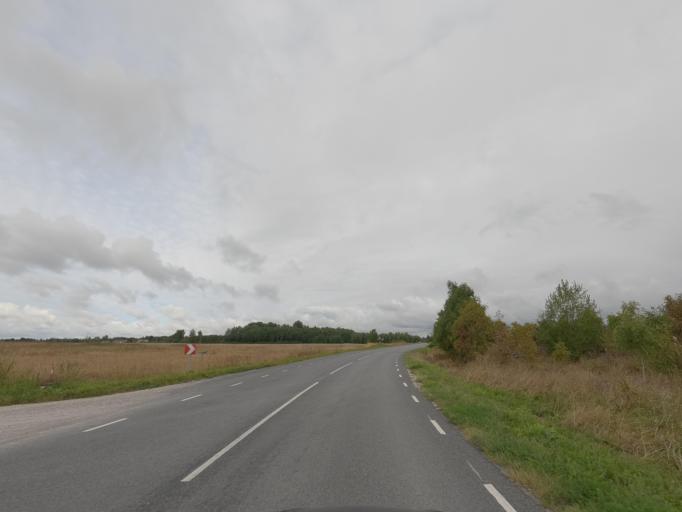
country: EE
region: Raplamaa
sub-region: Maerjamaa vald
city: Marjamaa
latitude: 59.0109
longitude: 24.5677
